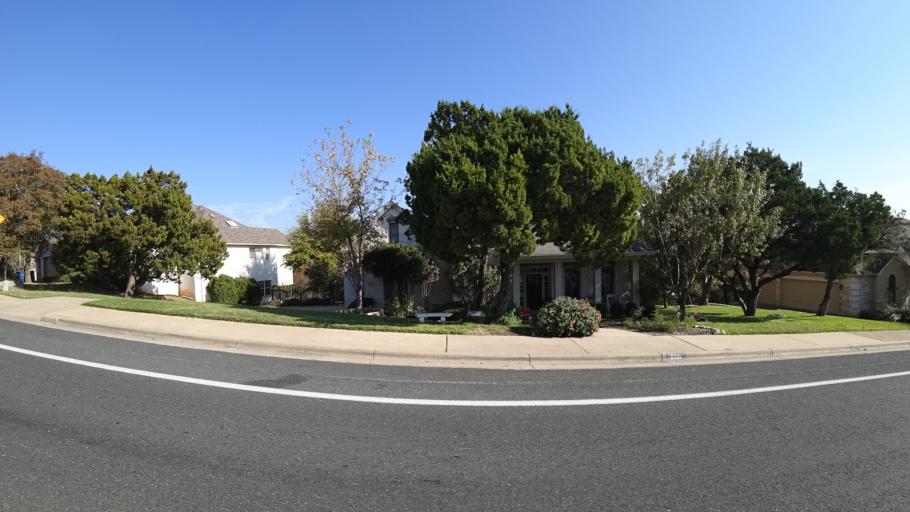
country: US
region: Texas
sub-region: Williamson County
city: Jollyville
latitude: 30.3905
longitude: -97.7692
